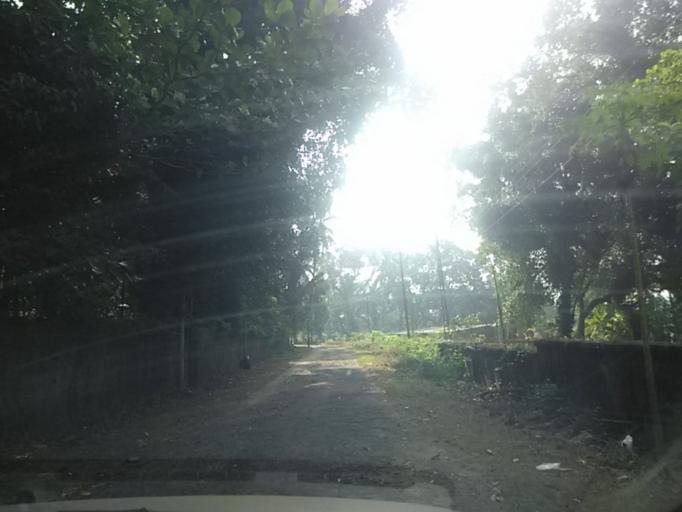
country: IN
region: Kerala
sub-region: Kozhikode
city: Mavoor
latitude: 11.3157
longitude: 75.9273
